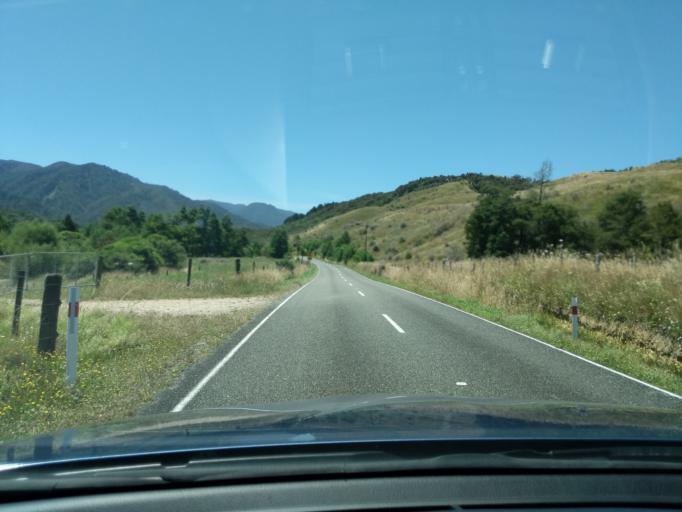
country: NZ
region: Tasman
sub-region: Tasman District
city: Takaka
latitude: -40.7368
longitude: 172.5809
